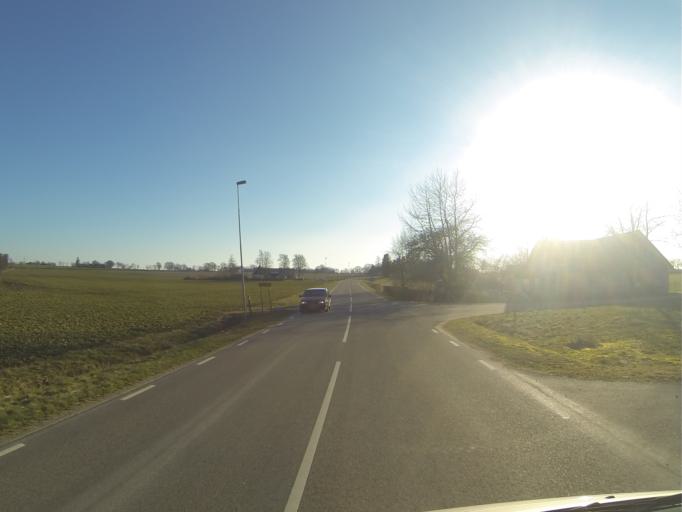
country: SE
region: Skane
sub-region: Horby Kommun
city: Hoerby
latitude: 55.8264
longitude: 13.6052
